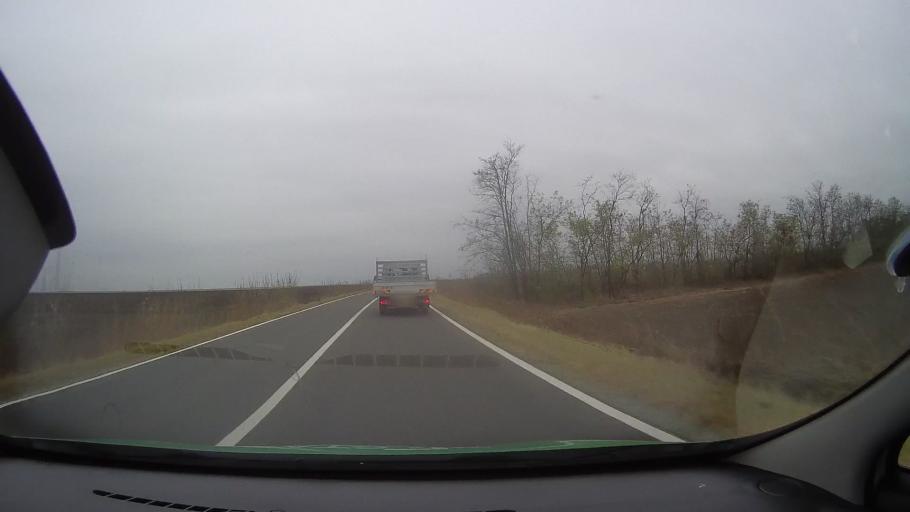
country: RO
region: Ialomita
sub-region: Comuna Gheorghe Lazar
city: Gheorghe Lazar
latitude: 44.6725
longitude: 27.4184
